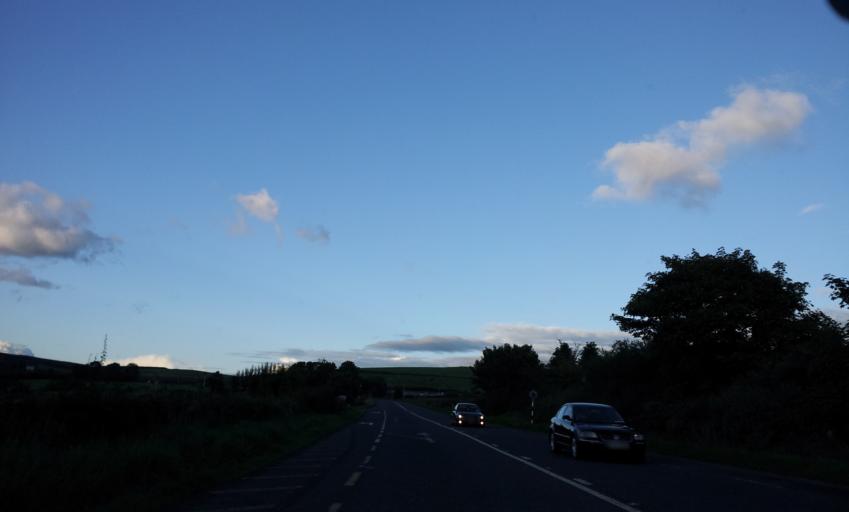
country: IE
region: Munster
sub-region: County Limerick
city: Newcastle West
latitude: 52.4090
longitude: -9.1603
